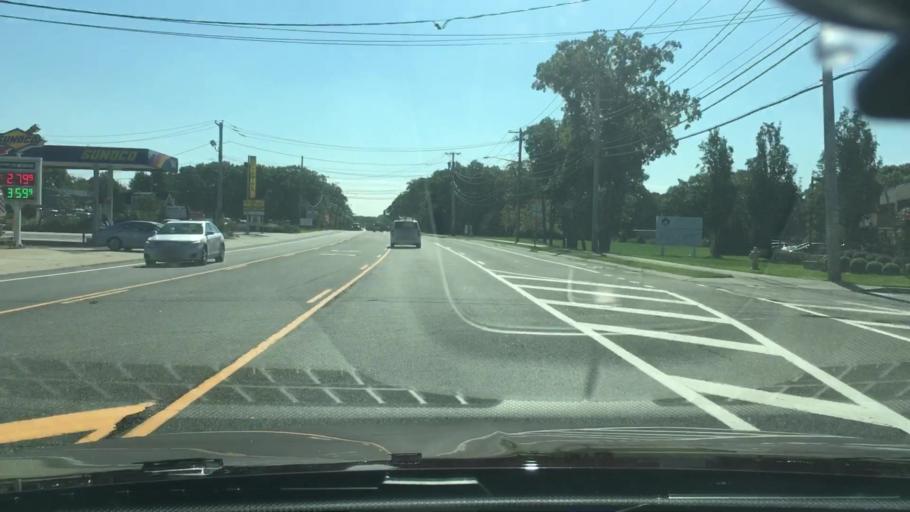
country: US
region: New York
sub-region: Suffolk County
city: Port Jefferson Station
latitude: 40.9109
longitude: -73.0297
